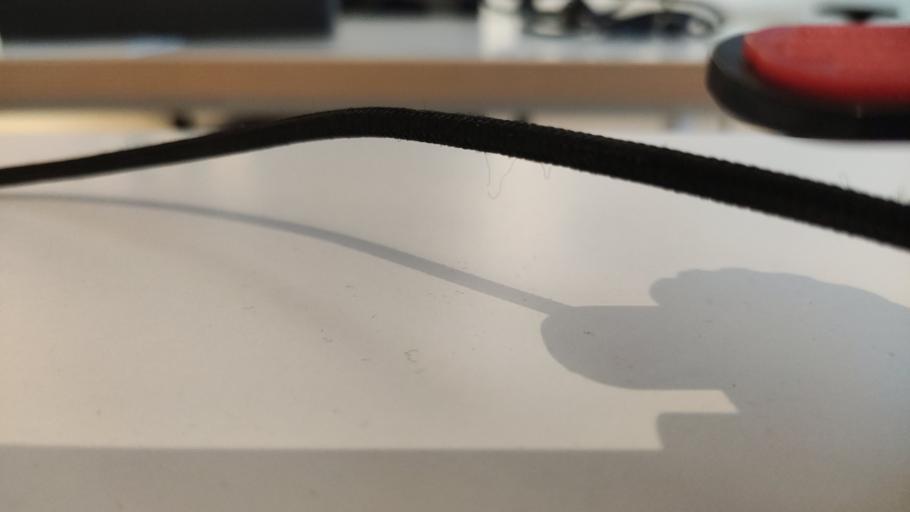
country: RU
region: Moskovskaya
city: Novopetrovskoye
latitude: 55.8572
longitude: 36.3775
